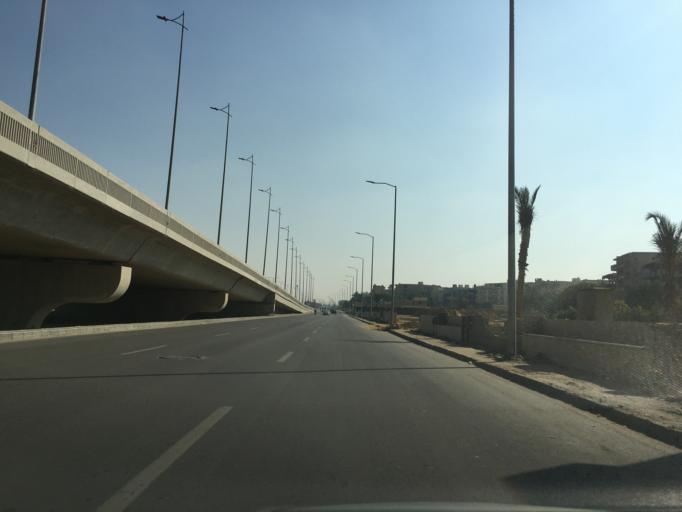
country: EG
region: Al Jizah
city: Awsim
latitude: 30.0069
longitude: 30.9829
